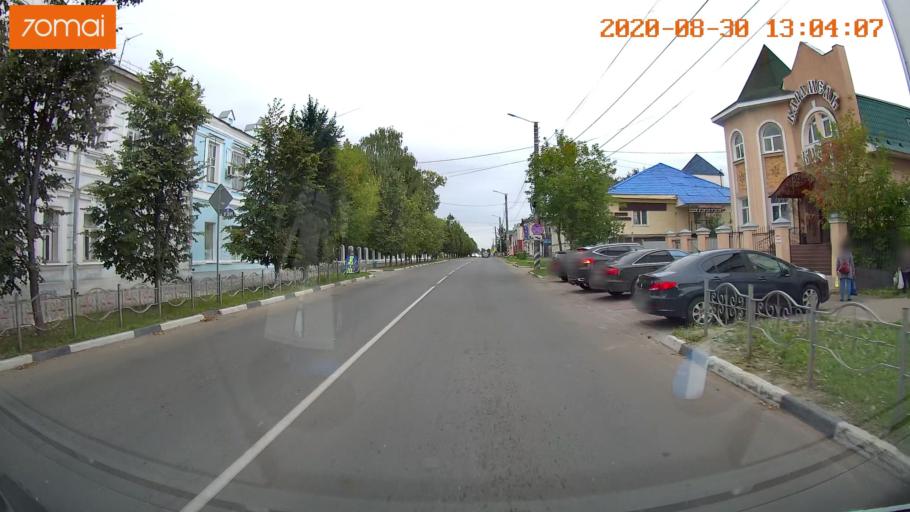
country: RU
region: Ivanovo
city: Kineshma
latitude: 57.4448
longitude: 42.1576
